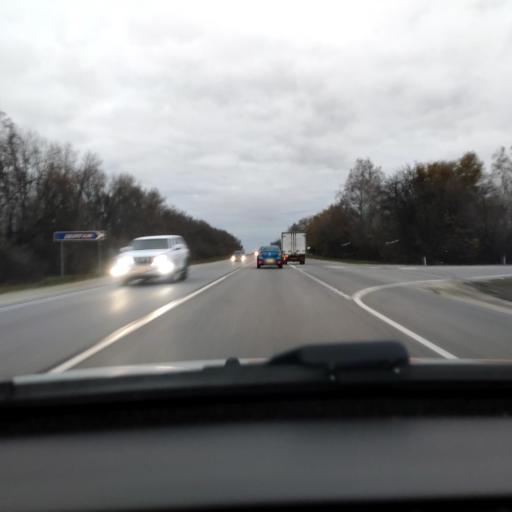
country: RU
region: Lipetsk
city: Borinskoye
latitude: 52.3912
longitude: 39.2291
